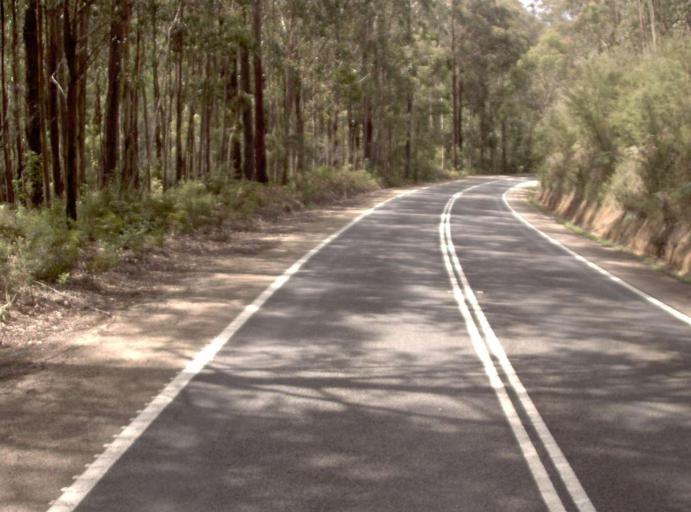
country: AU
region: New South Wales
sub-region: Bombala
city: Bombala
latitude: -37.5383
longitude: 149.3681
